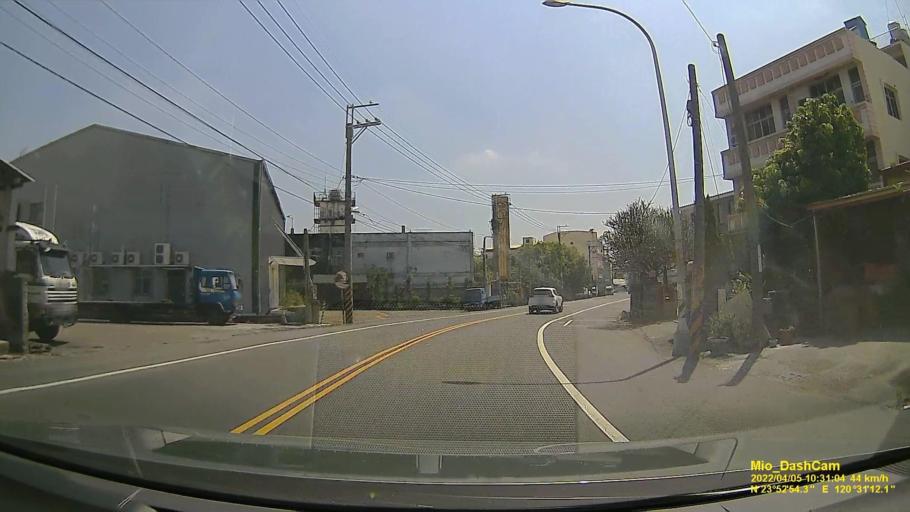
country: TW
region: Taiwan
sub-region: Nantou
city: Nantou
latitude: 23.8817
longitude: 120.5200
